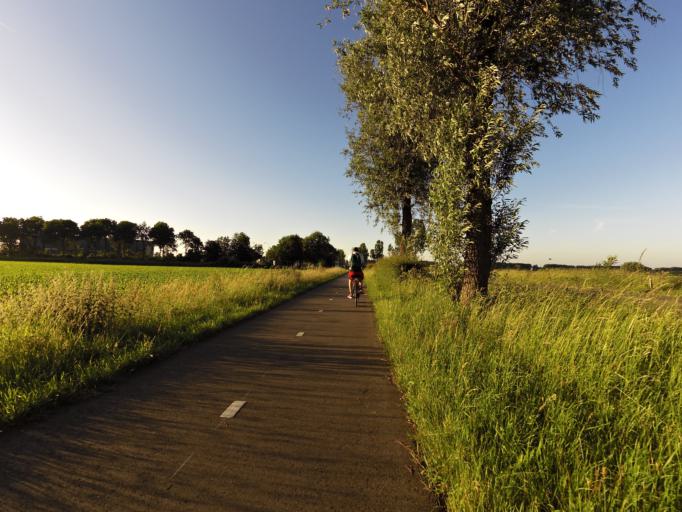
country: NL
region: Gelderland
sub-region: Gemeente Zevenaar
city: Zevenaar
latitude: 51.9618
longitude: 6.0846
